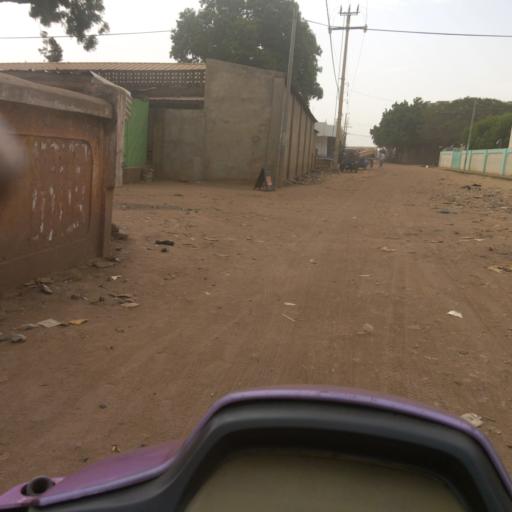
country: ML
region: Bamako
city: Bamako
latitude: 12.6651
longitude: -7.9450
